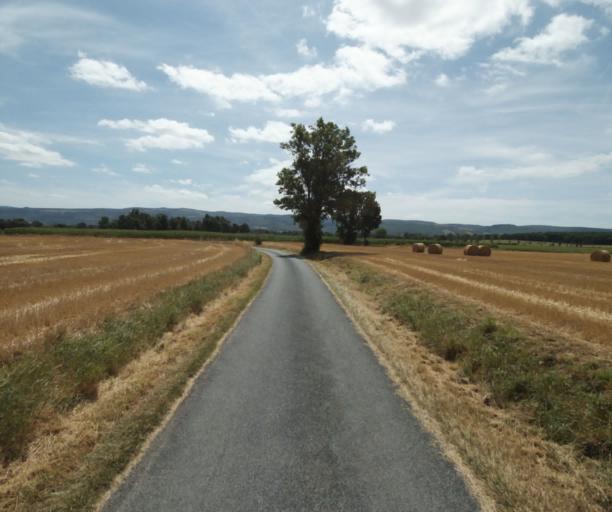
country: FR
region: Midi-Pyrenees
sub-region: Departement du Tarn
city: Soreze
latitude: 43.5019
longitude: 2.0741
